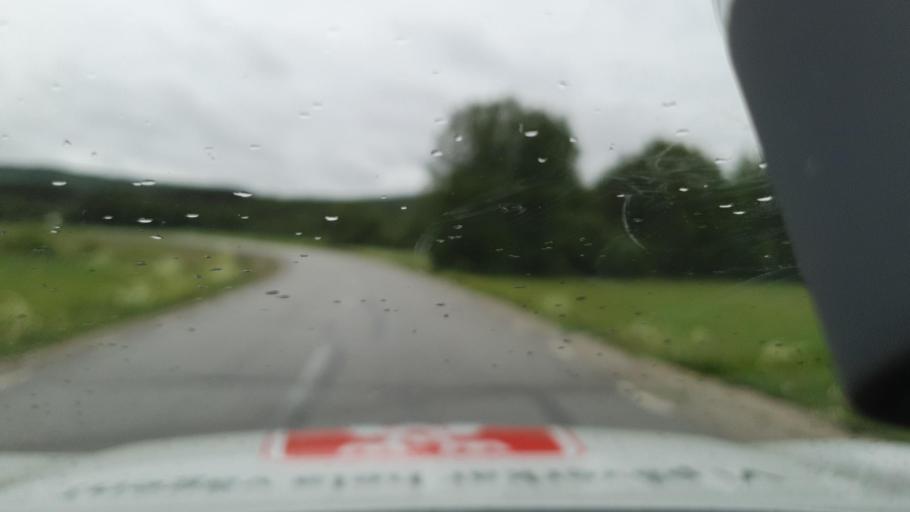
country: SE
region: Vaesterbotten
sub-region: Asele Kommun
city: Asele
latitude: 64.0109
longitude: 17.2553
